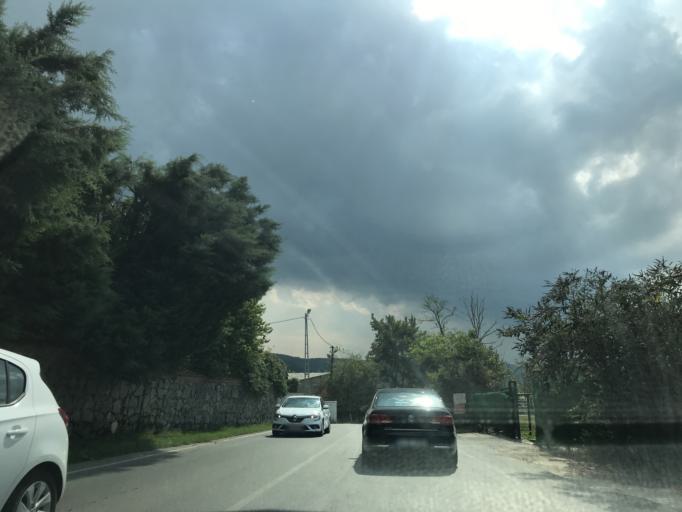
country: TR
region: Istanbul
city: Arikoey
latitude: 41.2131
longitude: 29.0345
